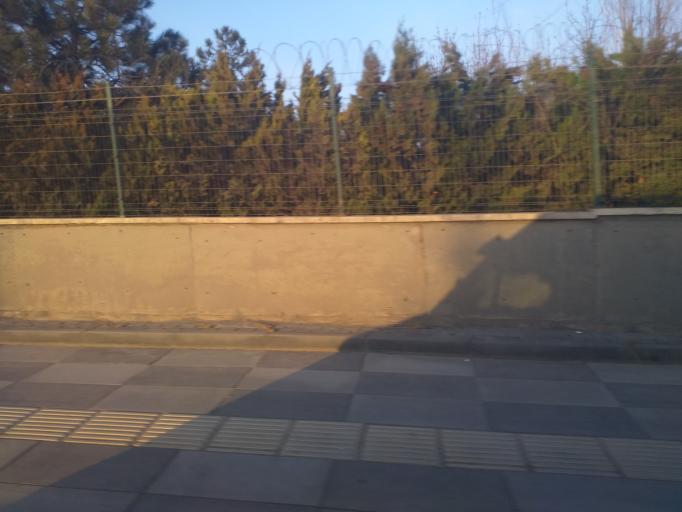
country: TR
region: Ankara
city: Ankara
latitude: 39.9520
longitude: 32.8229
